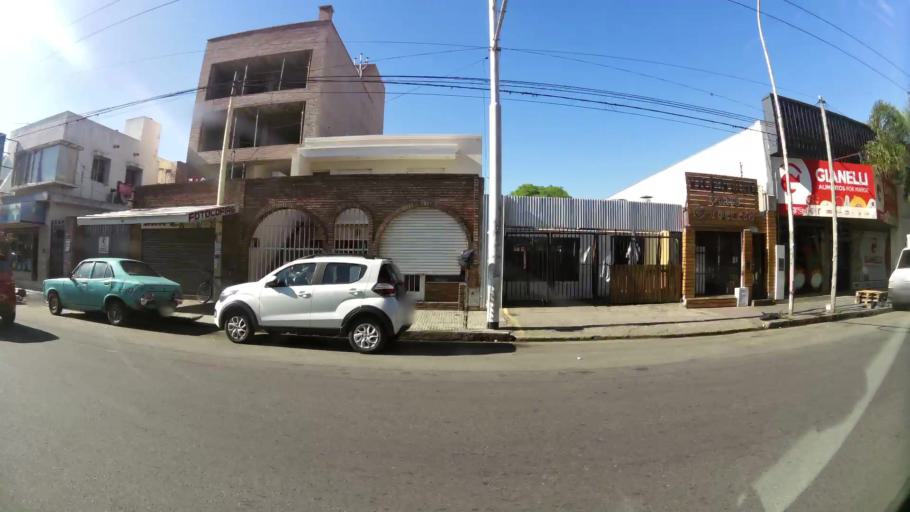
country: AR
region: Cordoba
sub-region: Departamento de Capital
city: Cordoba
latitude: -31.4239
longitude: -64.1424
